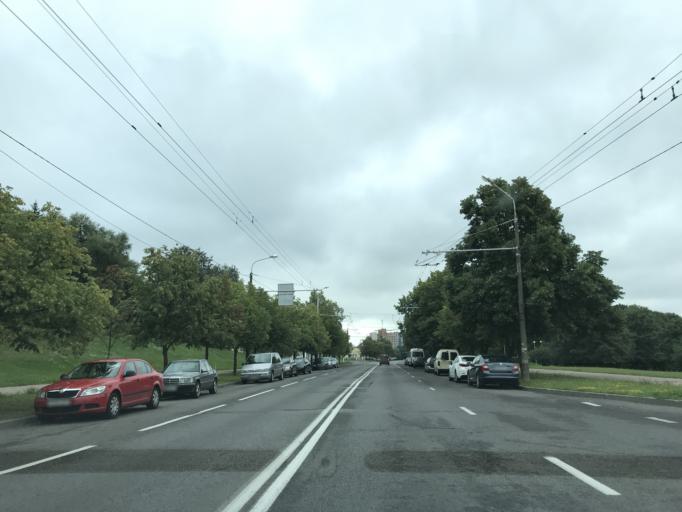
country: BY
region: Minsk
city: Borovlyany
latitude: 53.9532
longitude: 27.6313
